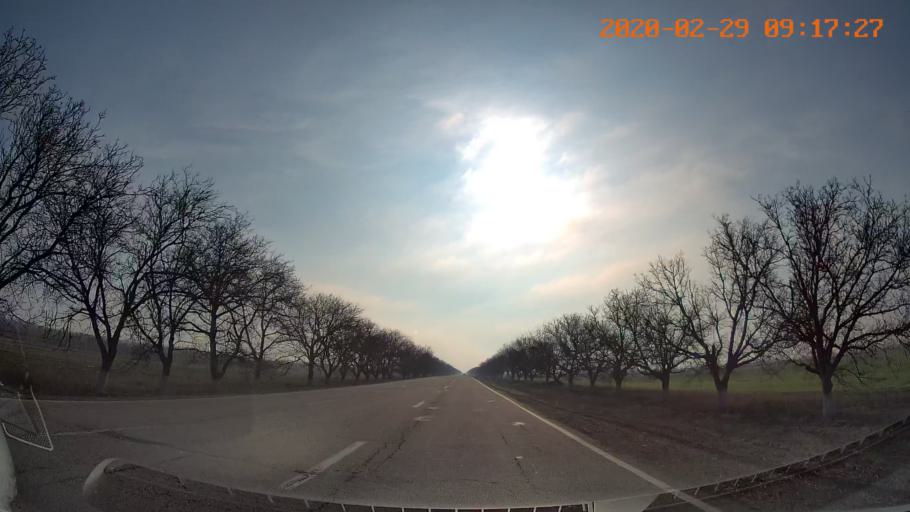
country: MD
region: Telenesti
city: Pervomaisc
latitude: 46.7829
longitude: 29.9044
